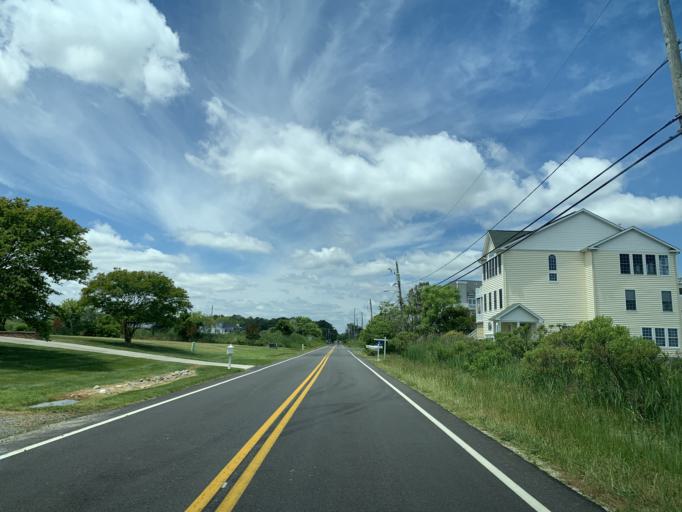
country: US
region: Maryland
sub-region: Worcester County
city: West Ocean City
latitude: 38.3307
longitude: -75.1020
